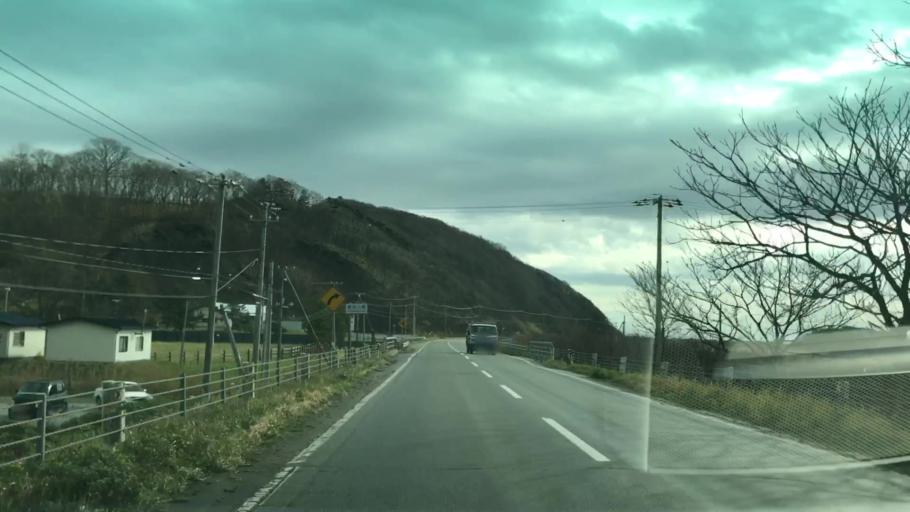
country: JP
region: Hokkaido
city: Shizunai-furukawacho
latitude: 42.1415
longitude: 142.8528
